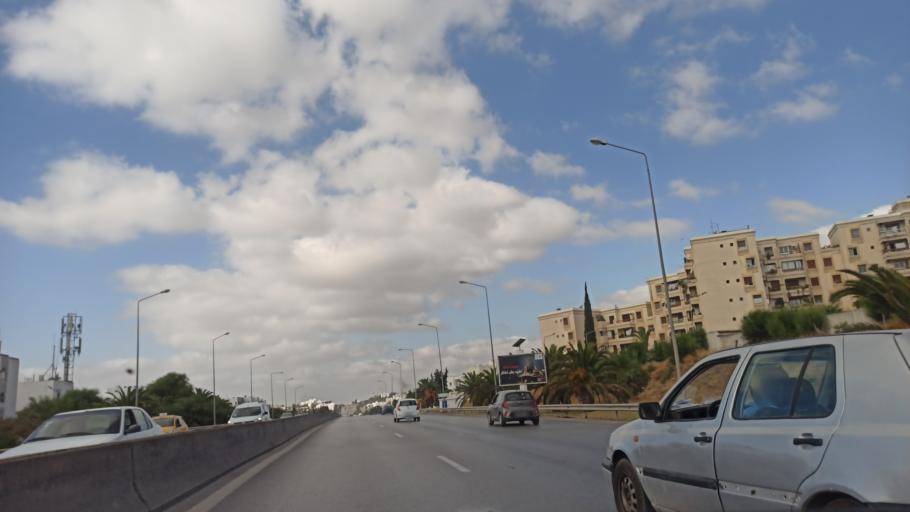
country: TN
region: Ariana
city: Ariana
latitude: 36.8454
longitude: 10.1787
